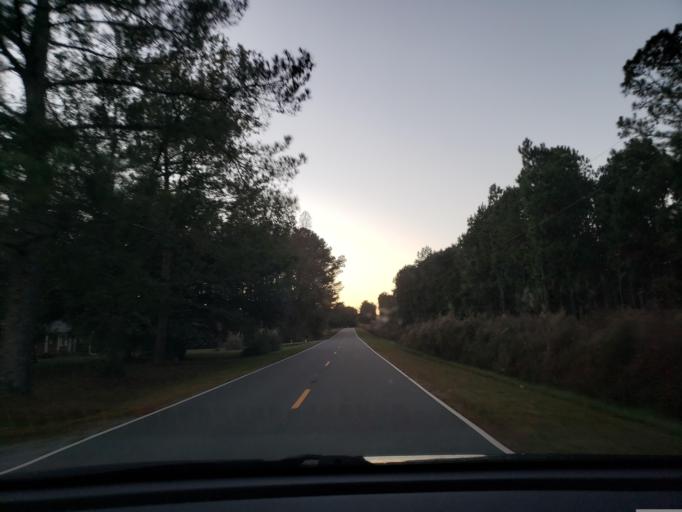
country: US
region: North Carolina
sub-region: Duplin County
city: Beulaville
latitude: 34.7653
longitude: -77.7271
